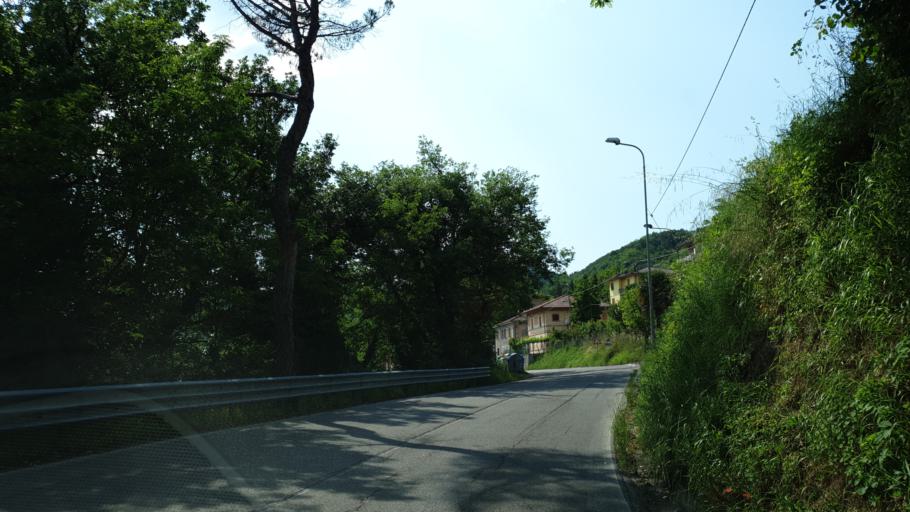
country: IT
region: Emilia-Romagna
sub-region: Forli-Cesena
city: Sarsina
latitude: 43.9241
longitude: 12.1583
